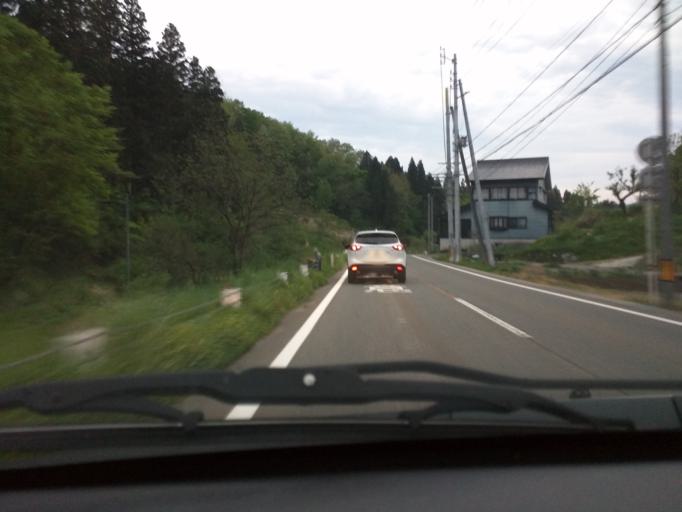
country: JP
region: Niigata
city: Ojiya
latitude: 37.3184
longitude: 138.7245
